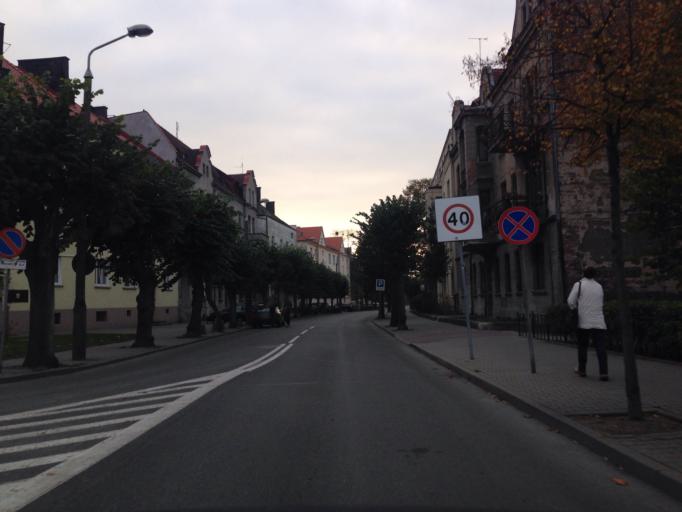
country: PL
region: Kujawsko-Pomorskie
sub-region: Powiat brodnicki
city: Brodnica
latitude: 53.2531
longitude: 19.3991
